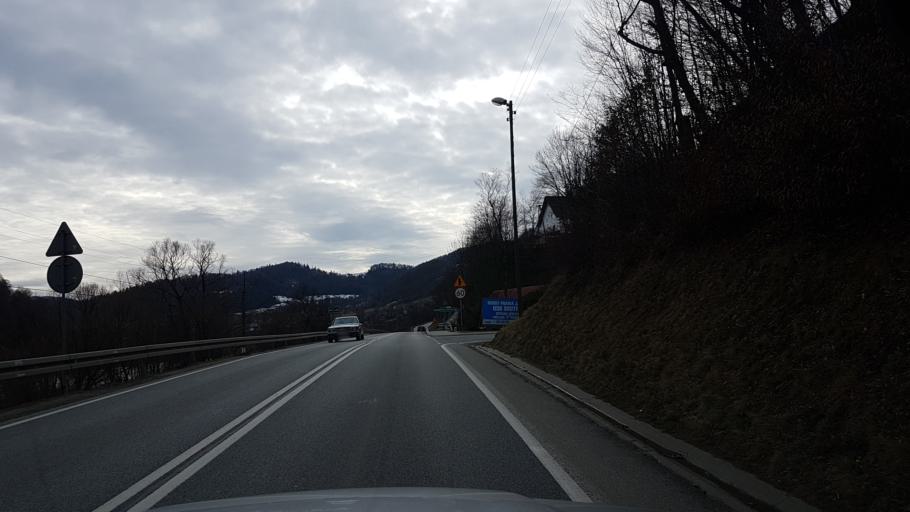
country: PL
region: Lesser Poland Voivodeship
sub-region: Powiat nowosadecki
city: Piwniczna-Zdroj
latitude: 49.4648
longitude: 20.6972
